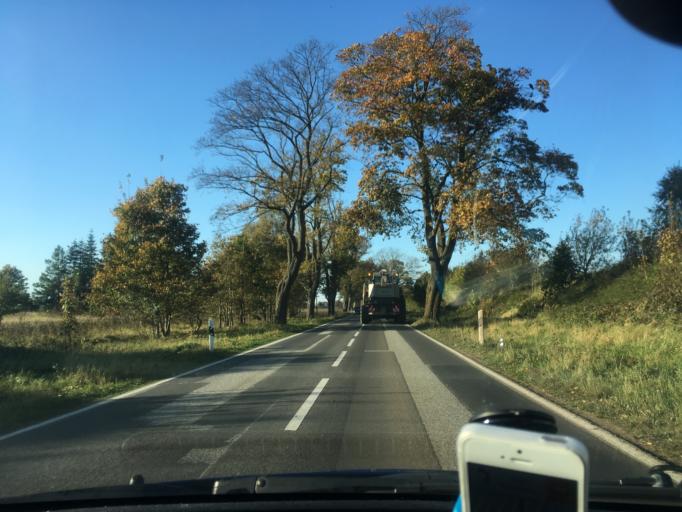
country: DE
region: Mecklenburg-Vorpommern
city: Zarrentin
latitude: 53.5369
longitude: 10.9388
